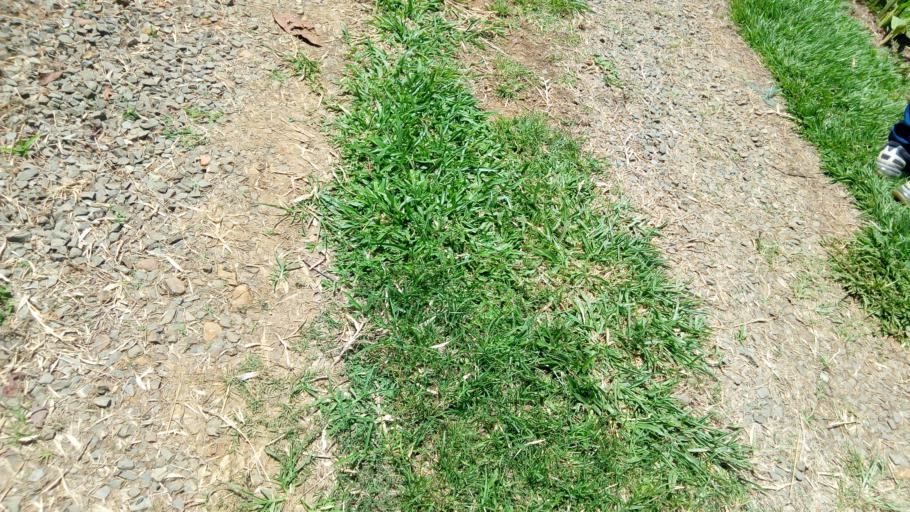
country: CO
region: Valle del Cauca
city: Cali
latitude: 3.4419
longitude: -76.5879
